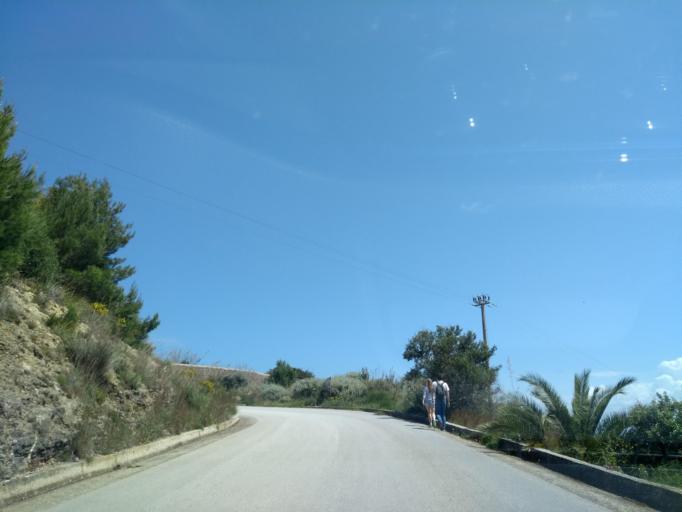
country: IT
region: Sicily
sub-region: Trapani
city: Castellammare del Golfo
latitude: 38.0568
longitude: 12.8363
